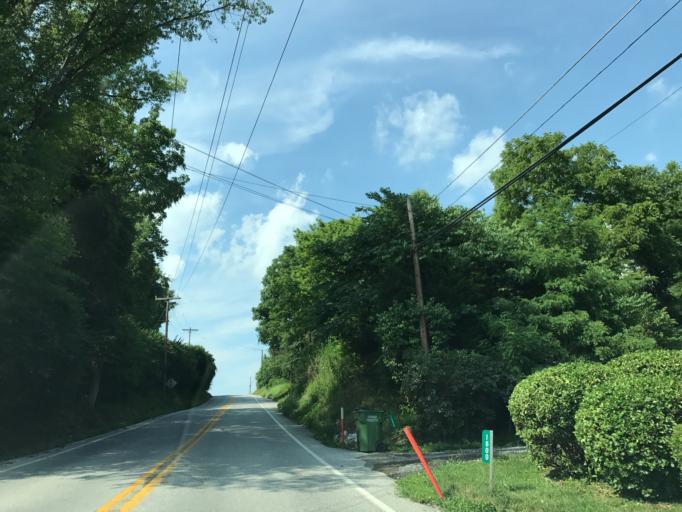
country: US
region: Pennsylvania
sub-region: York County
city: Pennville
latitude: 39.7606
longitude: -76.9935
